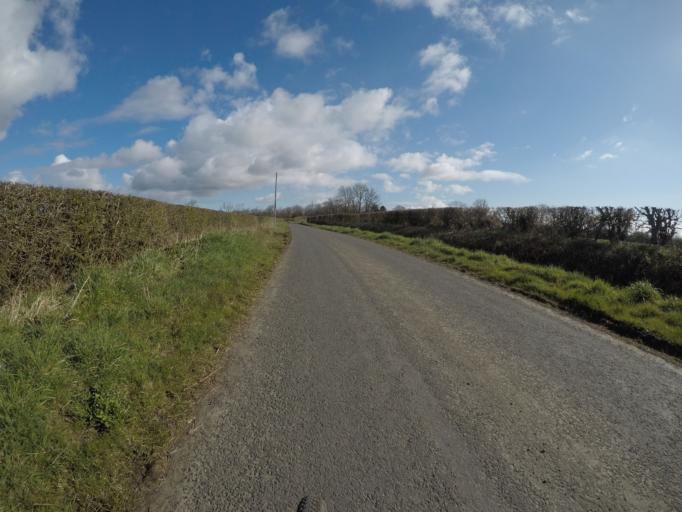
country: GB
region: Scotland
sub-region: North Ayrshire
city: Irvine
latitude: 55.6609
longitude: -4.6513
